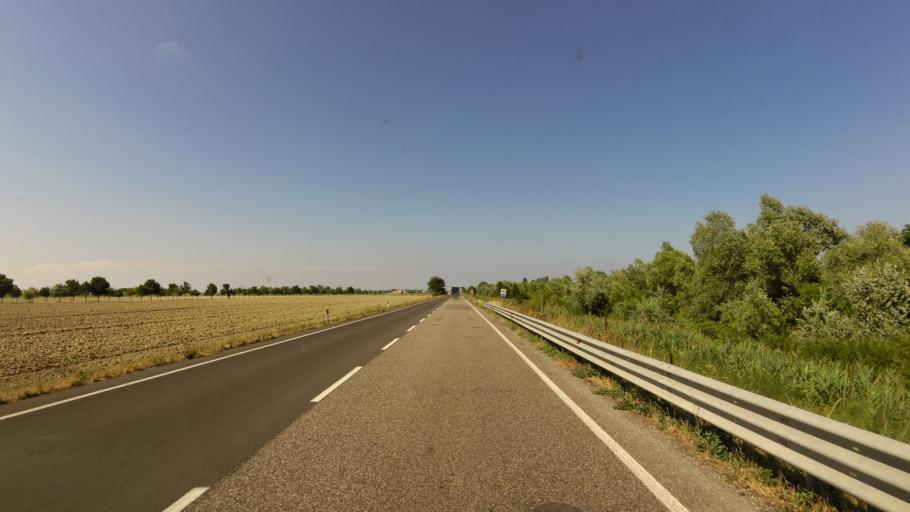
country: IT
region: Emilia-Romagna
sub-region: Provincia di Ravenna
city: Marina Romea
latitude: 44.5506
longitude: 12.2416
